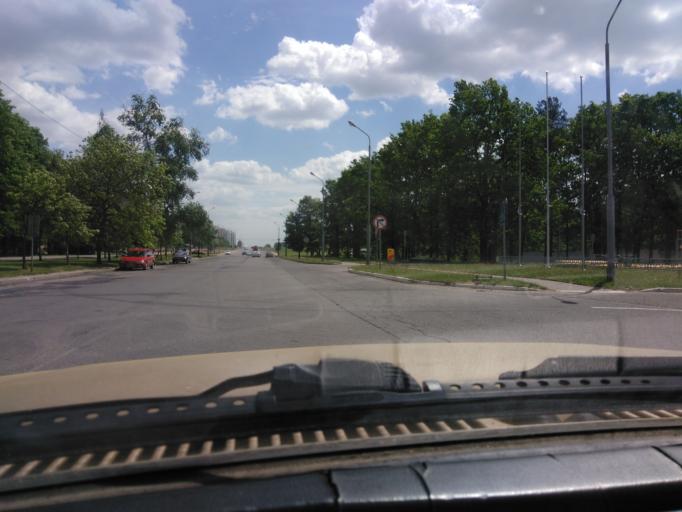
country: BY
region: Mogilev
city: Mahilyow
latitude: 53.9475
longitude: 30.3540
